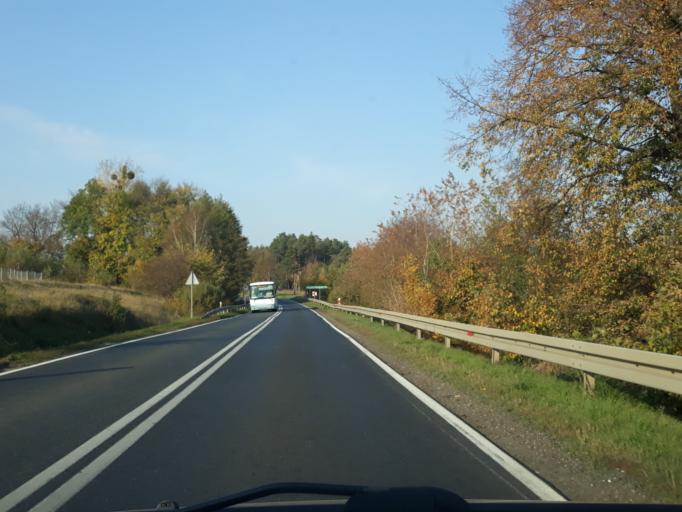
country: PL
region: Kujawsko-Pomorskie
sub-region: Powiat sepolenski
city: Sepolno Krajenskie
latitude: 53.4685
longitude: 17.5273
